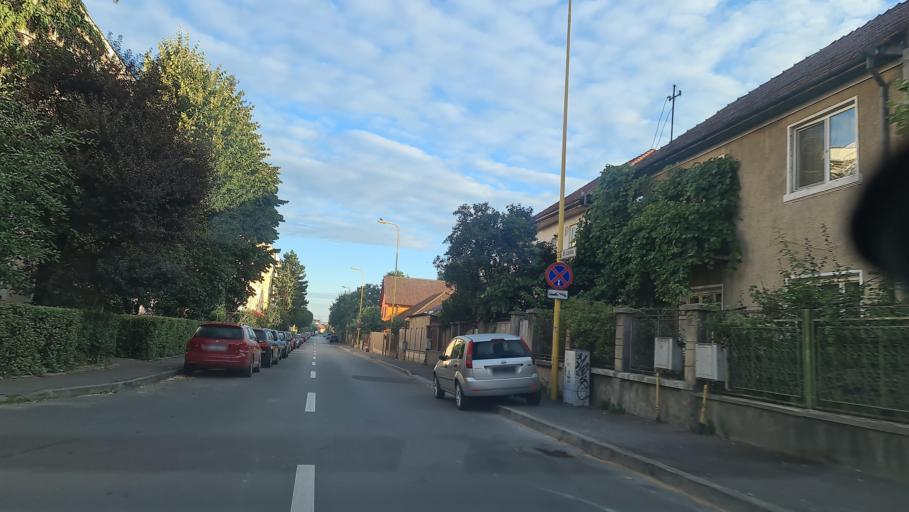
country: RO
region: Brasov
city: Brasov
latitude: 45.6533
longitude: 25.6304
